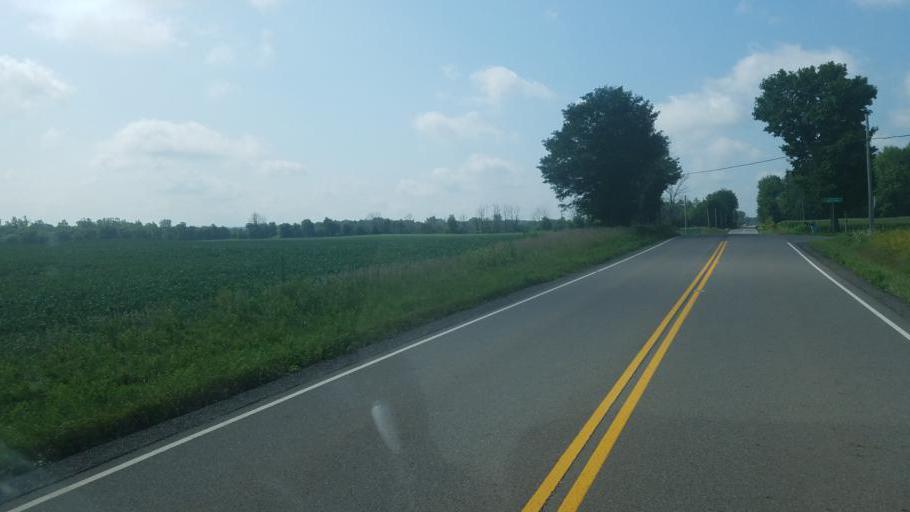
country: US
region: Ohio
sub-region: Licking County
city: Utica
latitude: 40.2805
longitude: -82.5148
